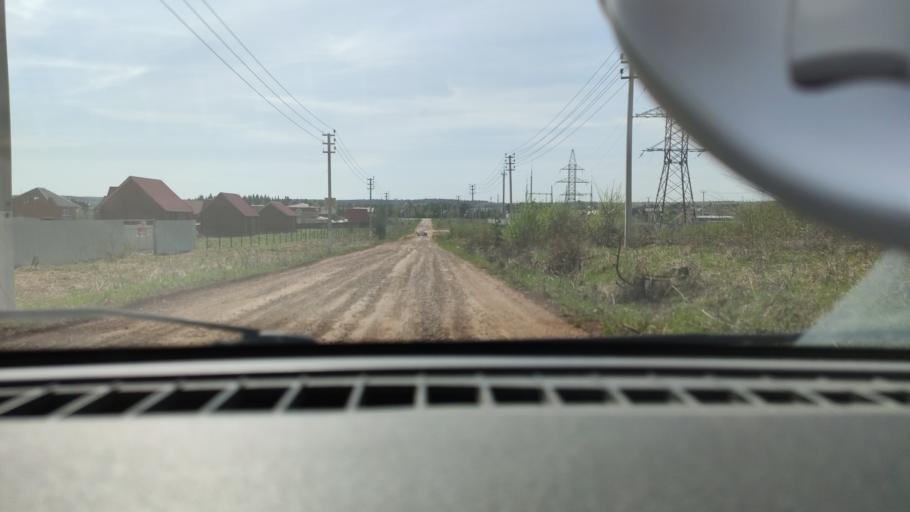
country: RU
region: Perm
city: Kultayevo
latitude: 57.8828
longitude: 55.8491
